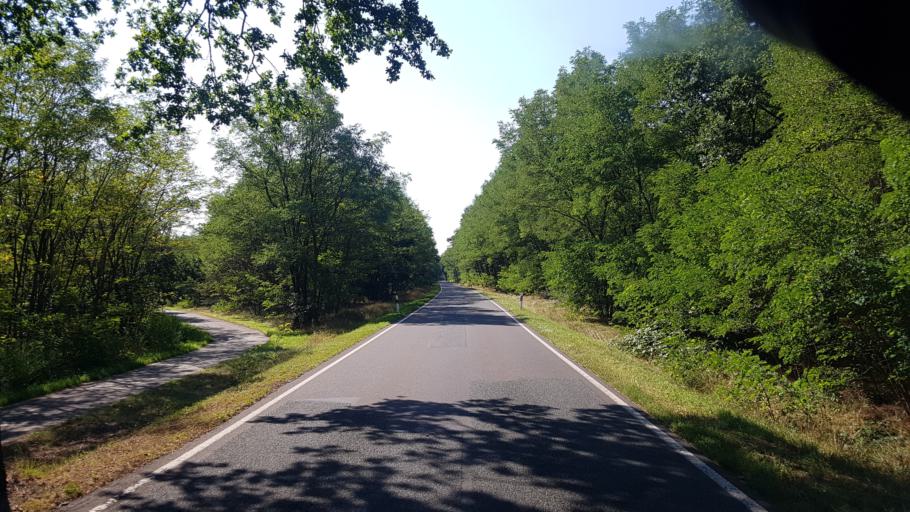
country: DE
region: Brandenburg
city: Altdobern
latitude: 51.7051
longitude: 14.0875
